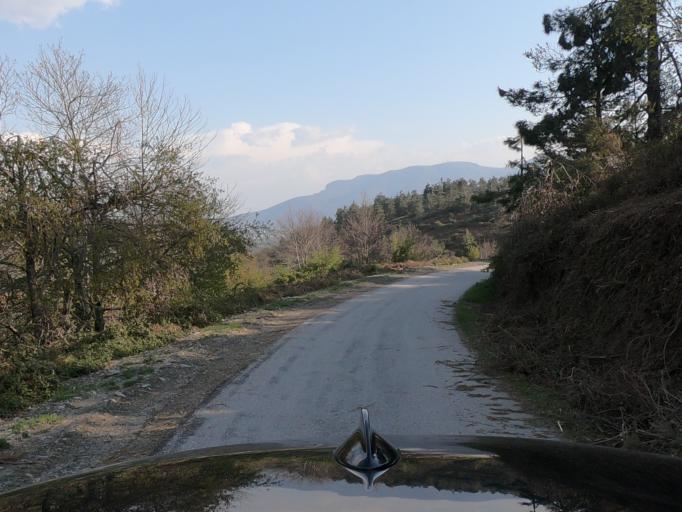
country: PT
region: Vila Real
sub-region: Vila Real
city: Vila Real
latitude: 41.3180
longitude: -7.8678
